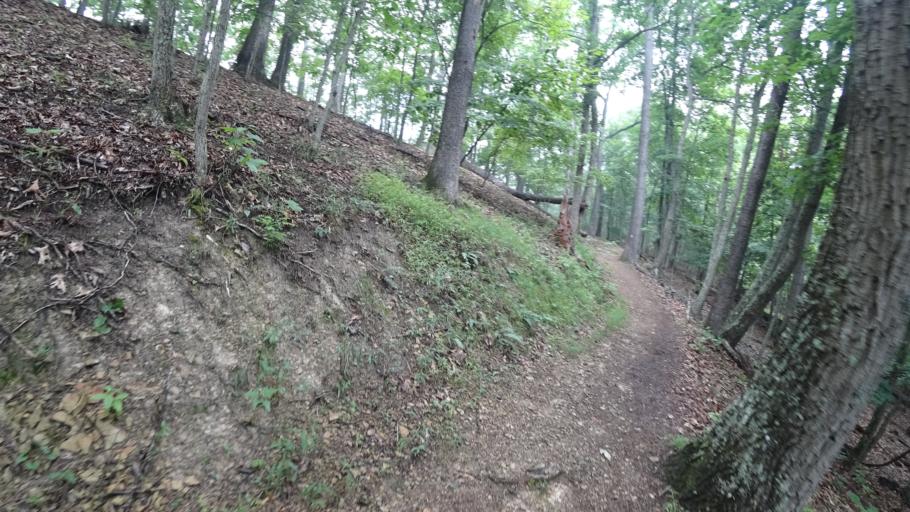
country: US
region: Virginia
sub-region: Smyth County
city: Marion
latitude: 36.8831
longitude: -81.5210
